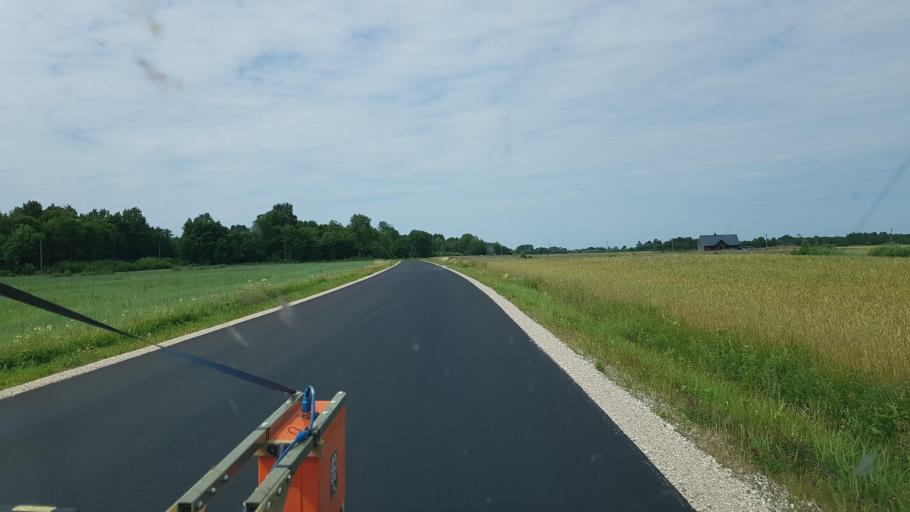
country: EE
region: Paernumaa
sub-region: Halinga vald
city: Parnu-Jaagupi
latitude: 58.6209
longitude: 24.3473
